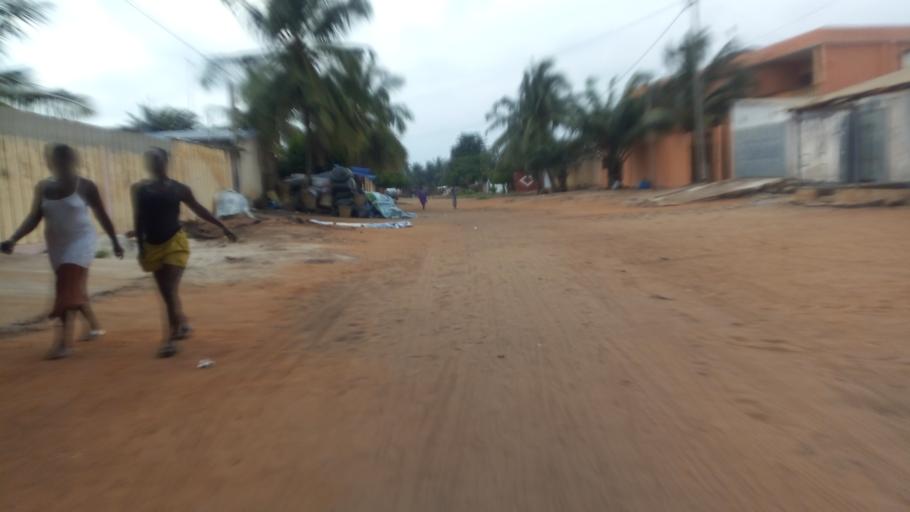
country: TG
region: Maritime
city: Lome
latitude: 6.1822
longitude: 1.1881
